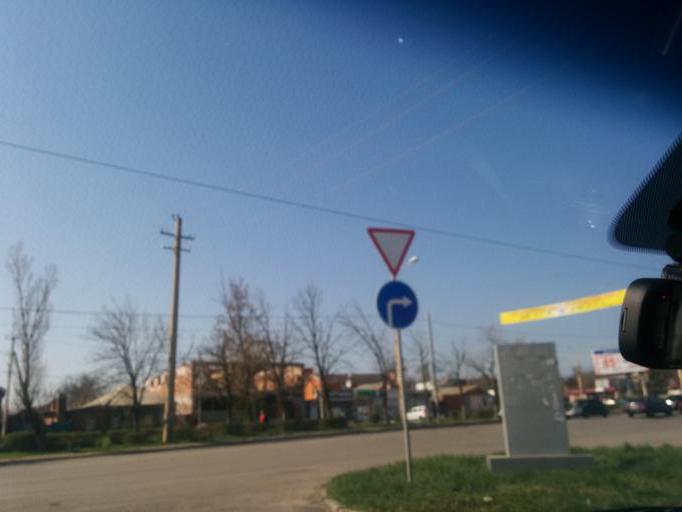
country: RU
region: Rostov
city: Shakhty
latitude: 47.6973
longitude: 40.2080
